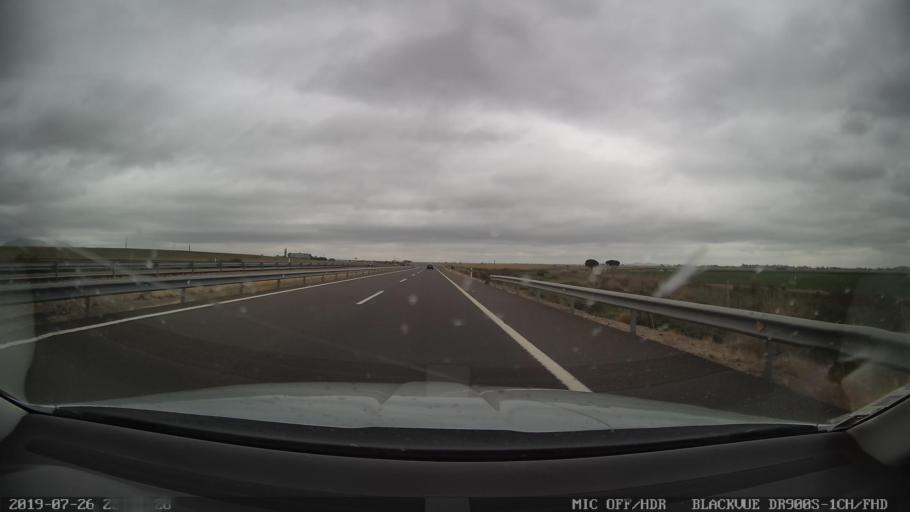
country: ES
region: Extremadura
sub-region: Provincia de Badajoz
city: Santa Amalia
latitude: 39.0685
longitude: -6.0447
